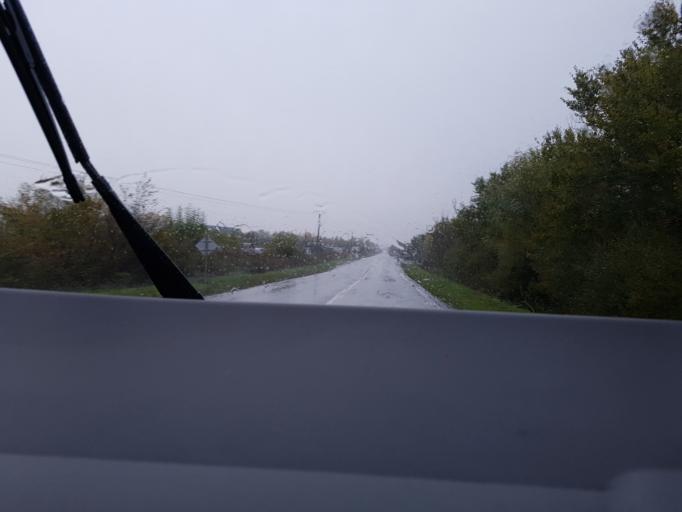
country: FR
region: Aquitaine
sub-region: Departement de la Gironde
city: Saint-Louis-de-Montferrand
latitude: 44.9385
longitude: -0.5240
